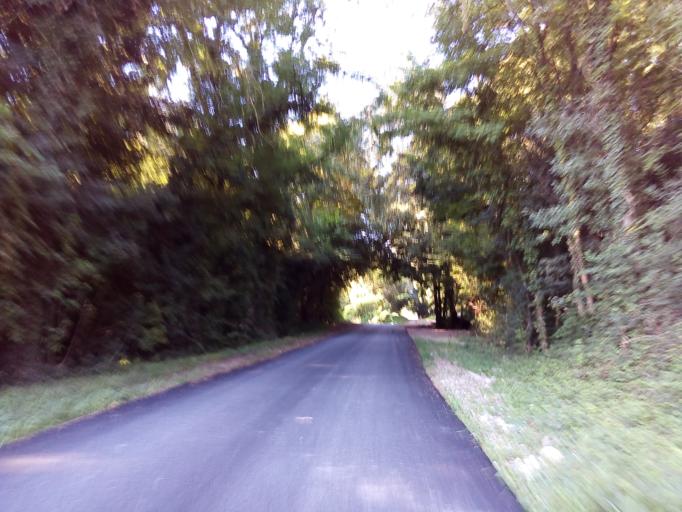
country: FR
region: Rhone-Alpes
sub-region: Departement de l'Isere
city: Saint-Vincent-de-Mercuze
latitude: 45.3617
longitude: 5.9674
